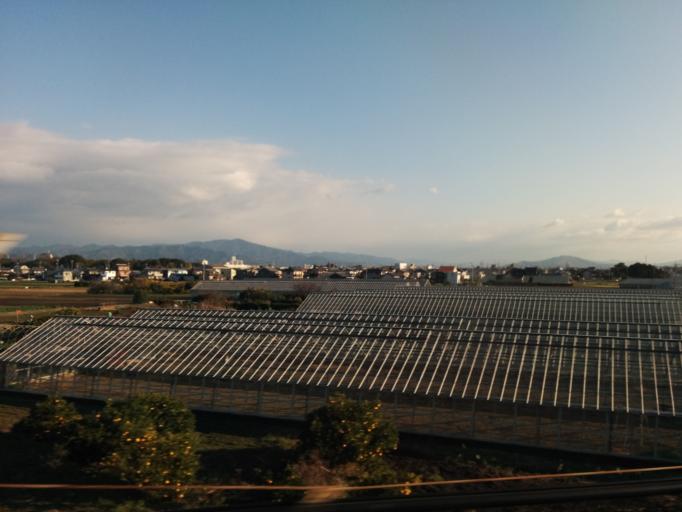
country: JP
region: Aichi
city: Kozakai-cho
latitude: 34.7913
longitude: 137.3454
